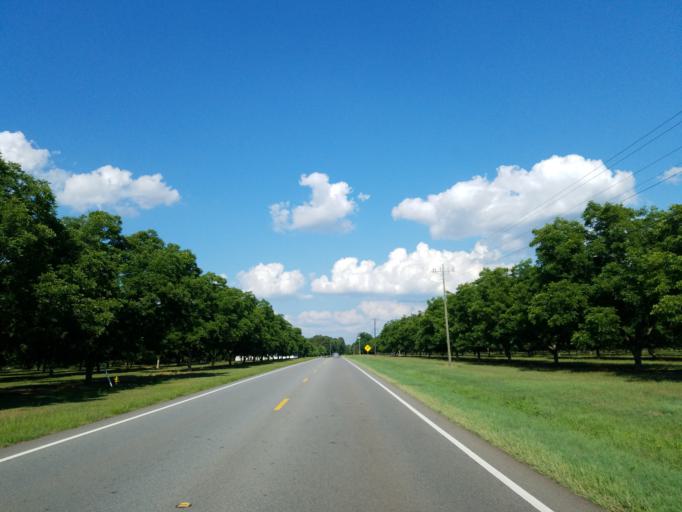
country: US
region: Georgia
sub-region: Peach County
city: Fort Valley
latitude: 32.5538
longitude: -83.7854
